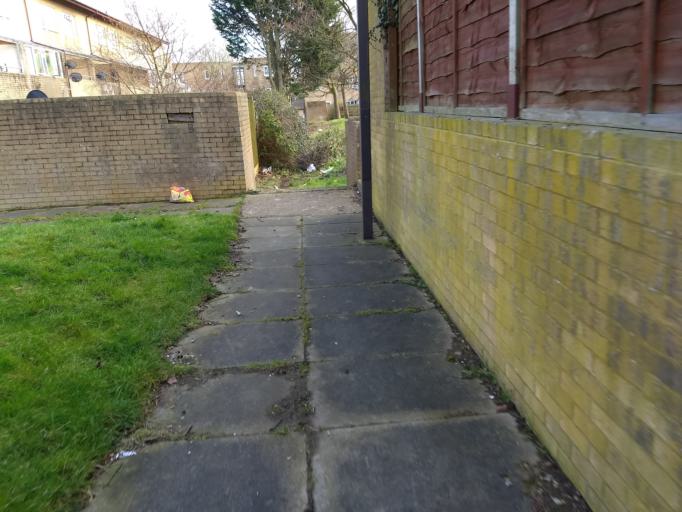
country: GB
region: England
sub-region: Milton Keynes
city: Milton Keynes
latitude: 52.0380
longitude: -0.7411
